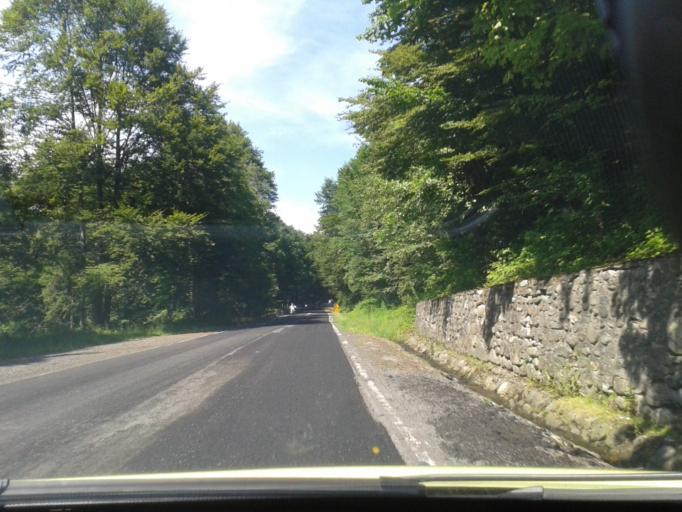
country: RO
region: Sibiu
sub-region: Comuna Cartisoara
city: Cartisoara
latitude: 45.6694
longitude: 24.5780
